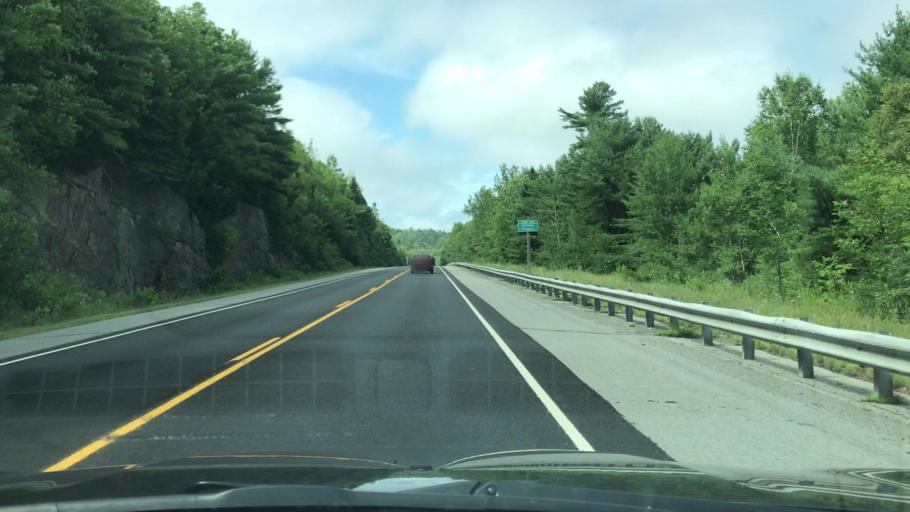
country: US
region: Maine
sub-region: Hancock County
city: Bucksport
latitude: 44.5492
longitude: -68.8094
